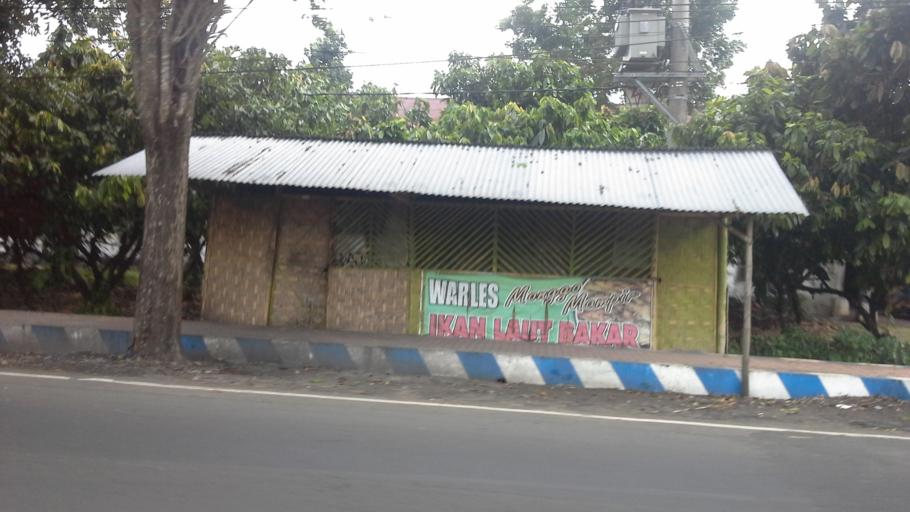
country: ID
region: East Java
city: Bondowoso
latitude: -7.9300
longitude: 113.8156
